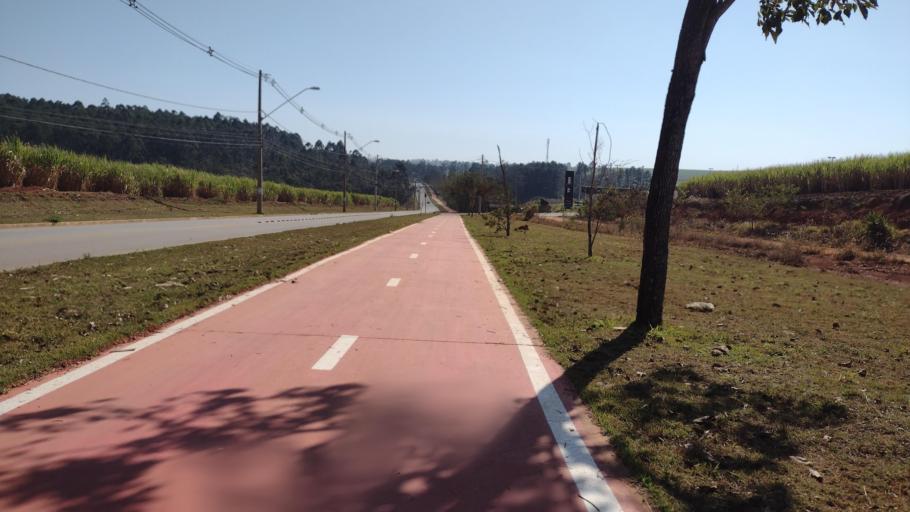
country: BR
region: Sao Paulo
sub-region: Sorocaba
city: Sorocaba
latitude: -23.3978
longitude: -47.4768
